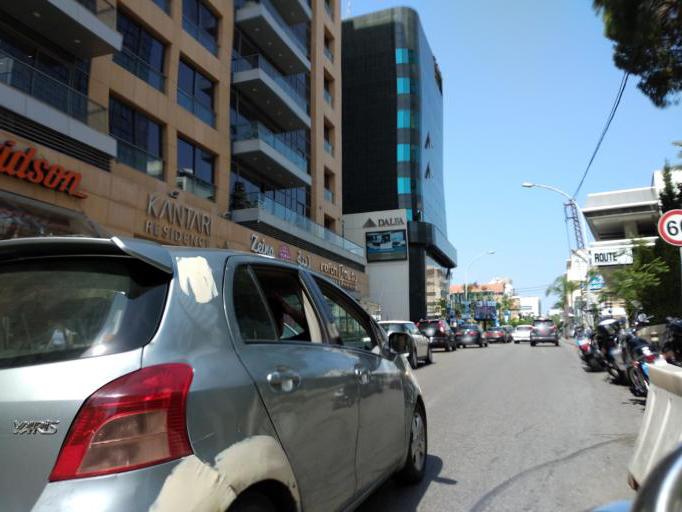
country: LB
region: Beyrouth
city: Beirut
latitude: 33.8953
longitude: 35.4919
